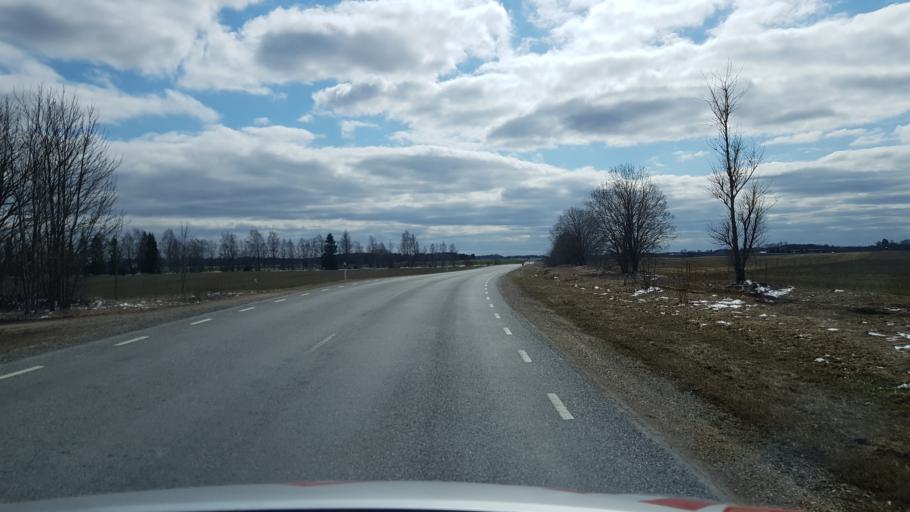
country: EE
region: Laeaene-Virumaa
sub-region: Tapa vald
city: Tapa
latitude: 59.3236
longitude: 26.0036
